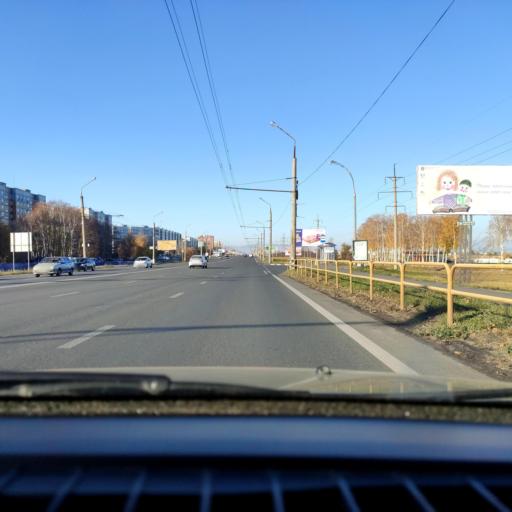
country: RU
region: Samara
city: Tol'yatti
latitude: 53.5473
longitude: 49.3610
